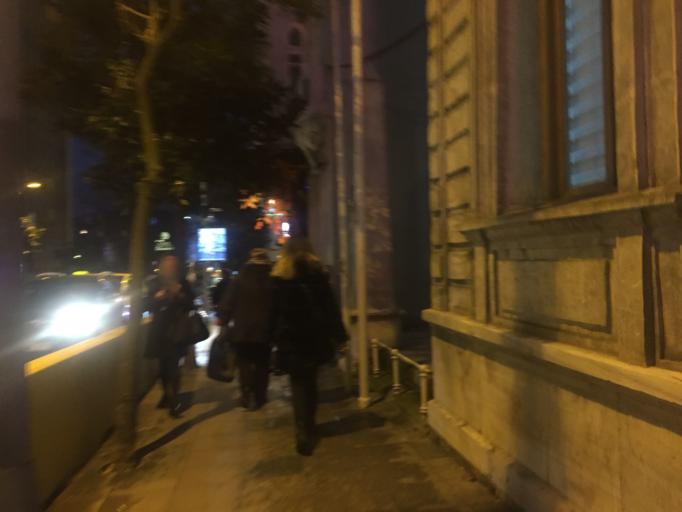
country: TR
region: Istanbul
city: Sisli
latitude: 41.0500
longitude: 28.9934
